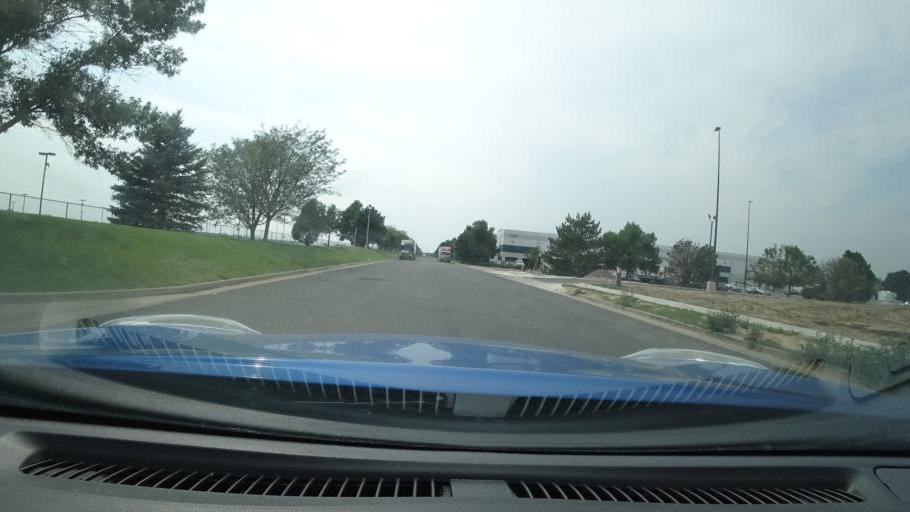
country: US
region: Colorado
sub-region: Adams County
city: Aurora
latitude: 39.7573
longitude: -104.7764
